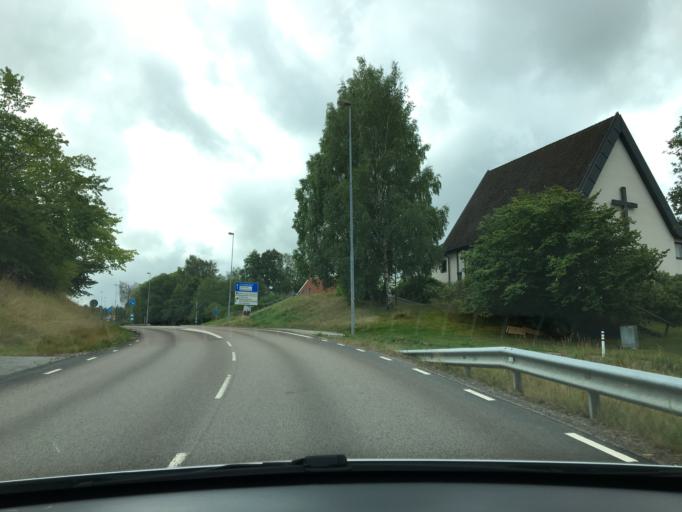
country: SE
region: Vaestra Goetaland
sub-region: Ale Kommun
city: Alvangen
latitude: 57.9573
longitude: 12.1245
